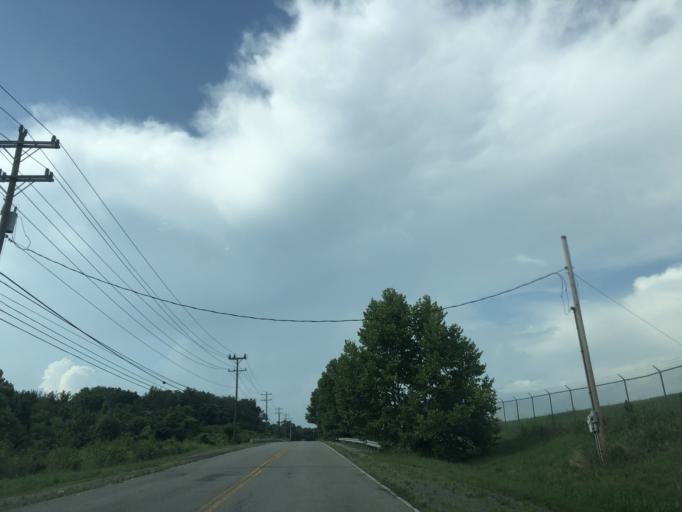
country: US
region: Tennessee
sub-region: Davidson County
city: Oak Hill
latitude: 36.1009
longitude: -86.6922
